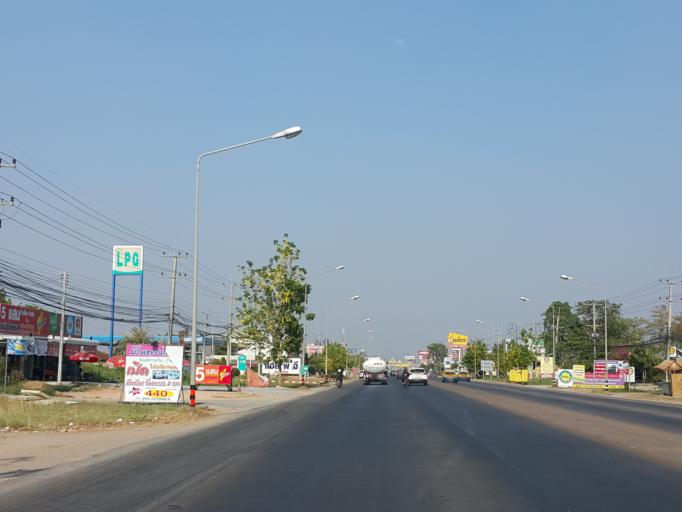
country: TH
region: Phitsanulok
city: Phitsanulok
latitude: 16.8165
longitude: 100.3088
